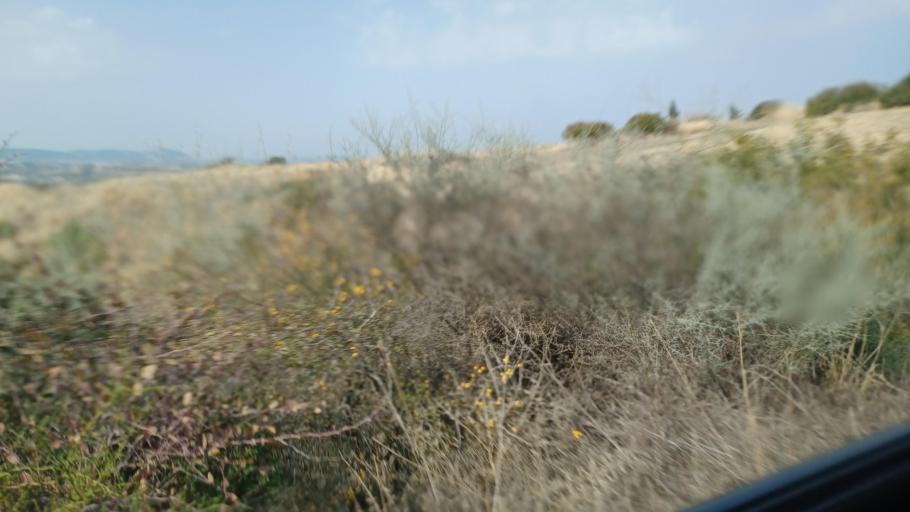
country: CY
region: Pafos
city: Polis
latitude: 34.9894
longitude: 32.4586
